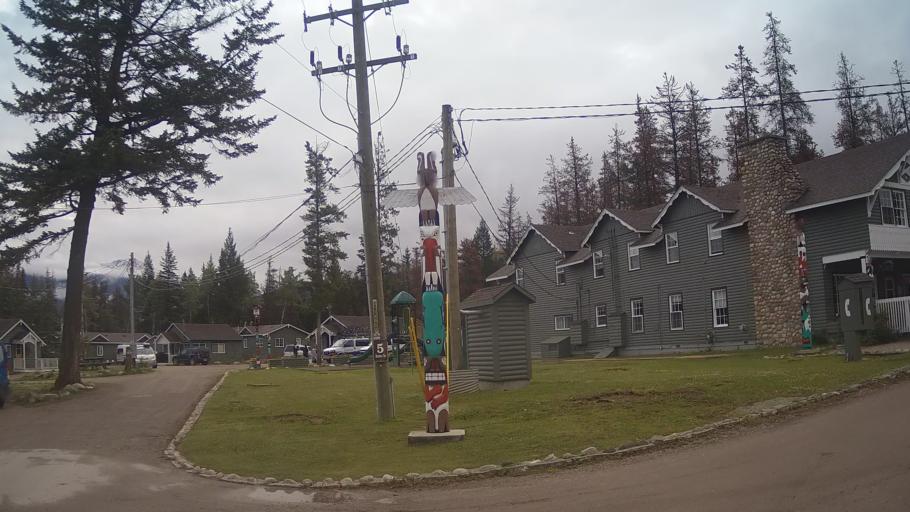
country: CA
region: Alberta
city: Jasper Park Lodge
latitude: 52.8669
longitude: -118.0690
